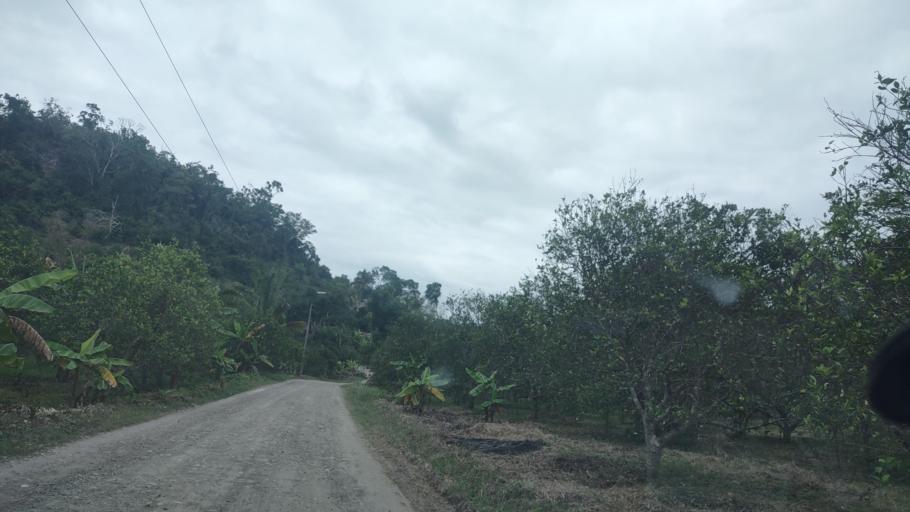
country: MX
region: Veracruz
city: Papantla de Olarte
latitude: 20.4331
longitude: -97.2642
